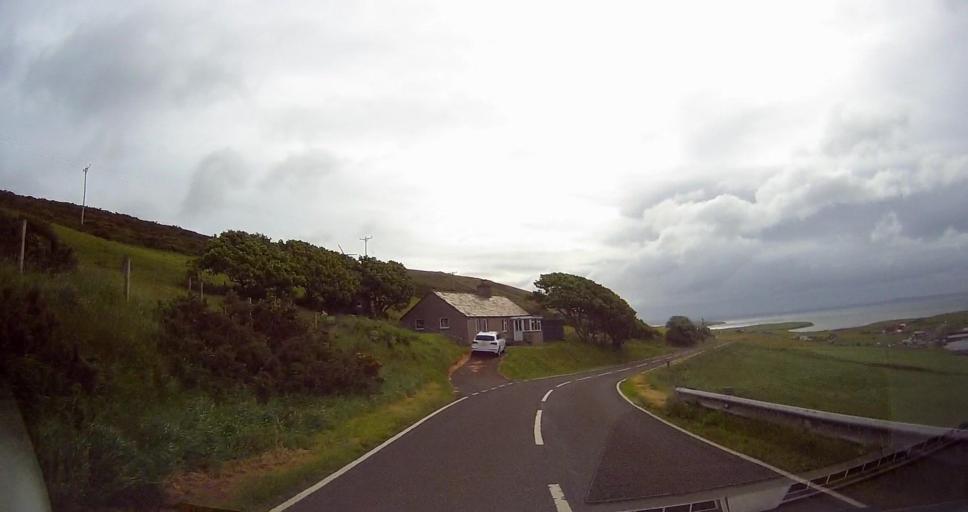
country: GB
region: Scotland
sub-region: Orkney Islands
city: Stromness
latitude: 58.9210
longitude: -3.1952
